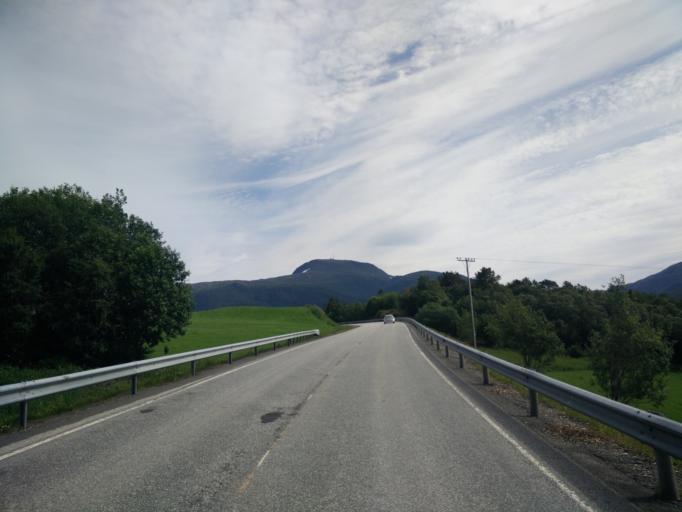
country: NO
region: More og Romsdal
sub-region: Kristiansund
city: Rensvik
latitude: 62.9712
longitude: 7.8090
